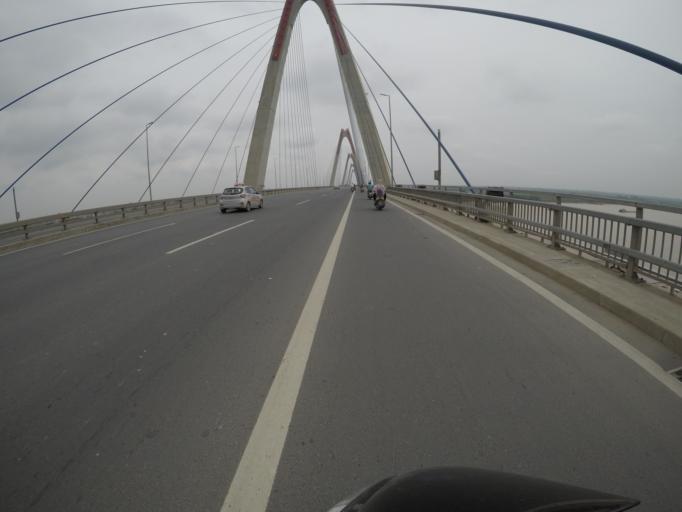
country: VN
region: Ha Noi
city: Tay Ho
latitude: 21.0884
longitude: 105.8188
